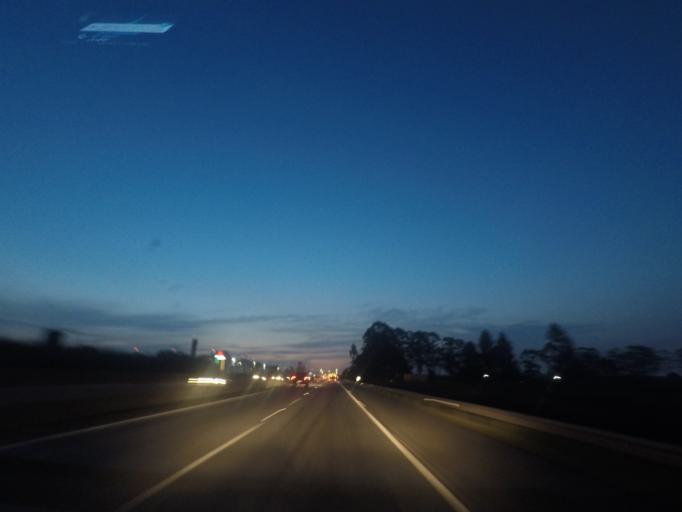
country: BR
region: Parana
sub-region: Pinhais
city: Pinhais
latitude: -25.4928
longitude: -49.1697
